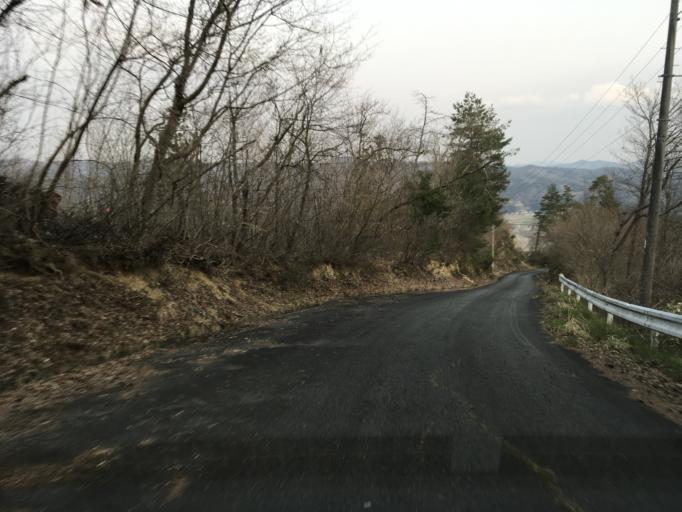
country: JP
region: Iwate
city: Ichinoseki
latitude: 38.9411
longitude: 141.2369
